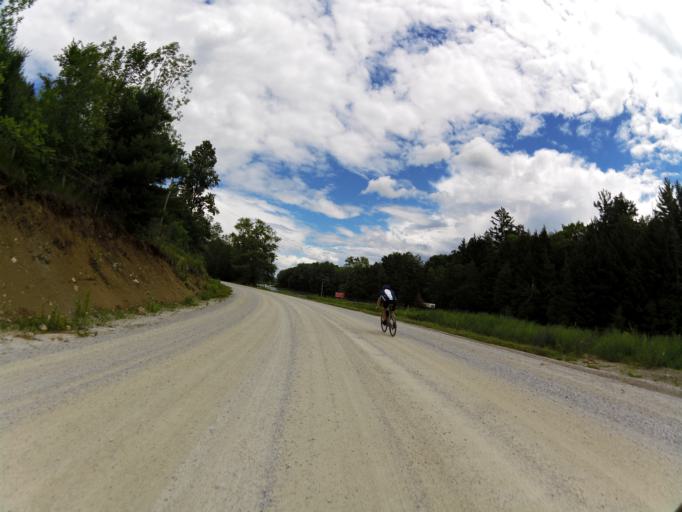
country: CA
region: Ontario
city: Renfrew
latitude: 45.1350
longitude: -76.6596
